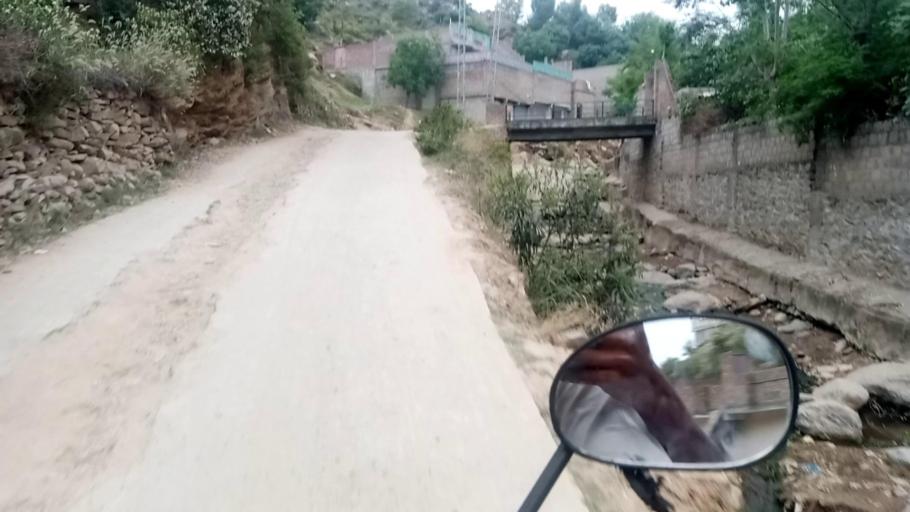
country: PK
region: Khyber Pakhtunkhwa
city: Saidu Sharif
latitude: 34.7629
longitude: 72.3546
